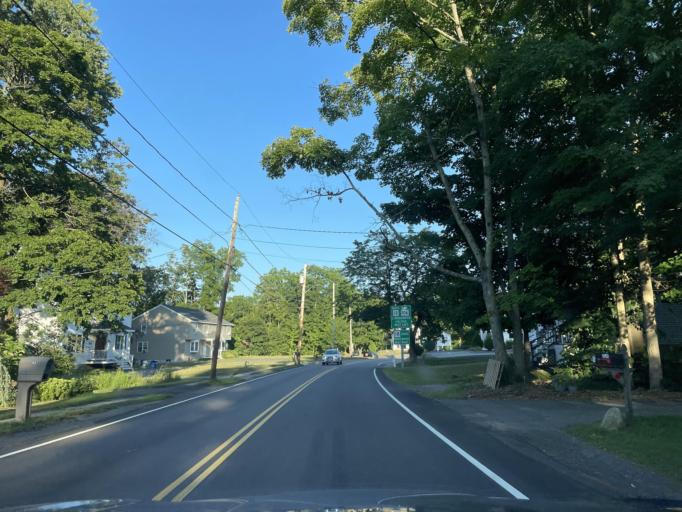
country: US
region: Massachusetts
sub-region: Plymouth County
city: East Bridgewater
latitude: 42.0148
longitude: -70.9635
